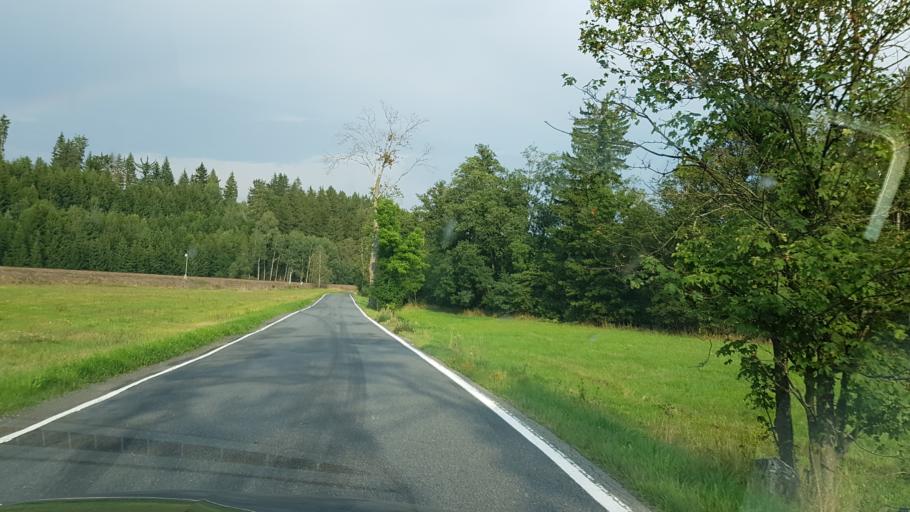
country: CZ
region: Pardubicky
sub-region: Okres Usti nad Orlici
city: Kraliky
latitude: 50.0858
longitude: 16.8301
